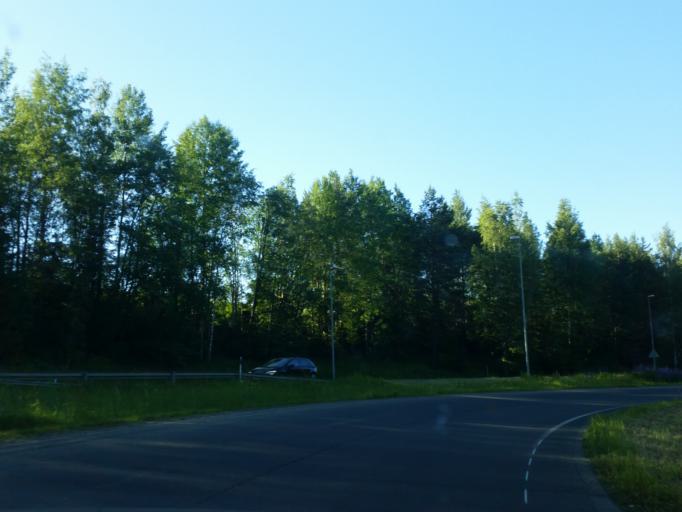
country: FI
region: Northern Savo
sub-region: Kuopio
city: Kuopio
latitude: 62.8851
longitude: 27.6336
